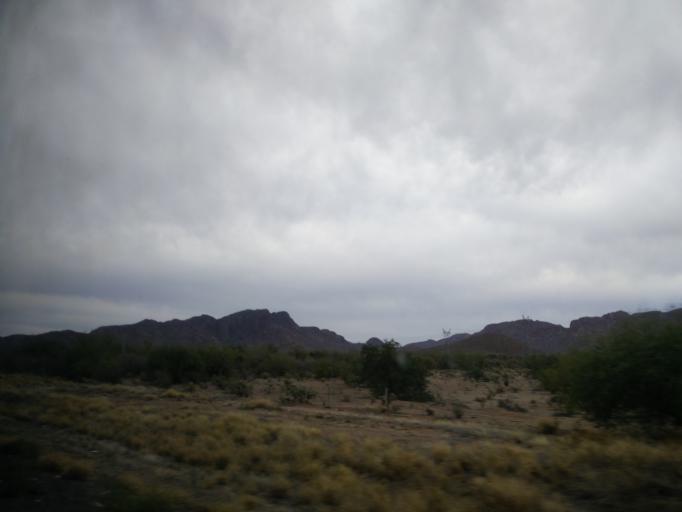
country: MX
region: Sonora
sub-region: Hermosillo
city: Miguel Aleman (La Doce)
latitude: 28.5721
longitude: -111.0314
